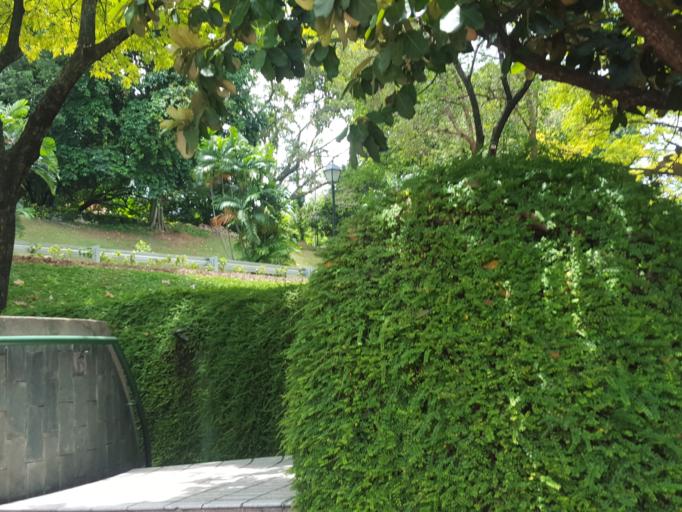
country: SG
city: Singapore
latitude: 1.2974
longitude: 103.8463
